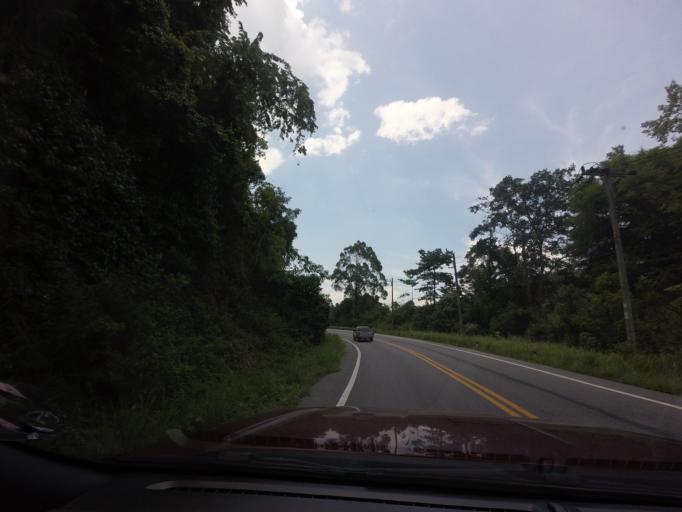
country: TH
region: Yala
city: Than To
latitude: 6.0383
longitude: 101.1968
